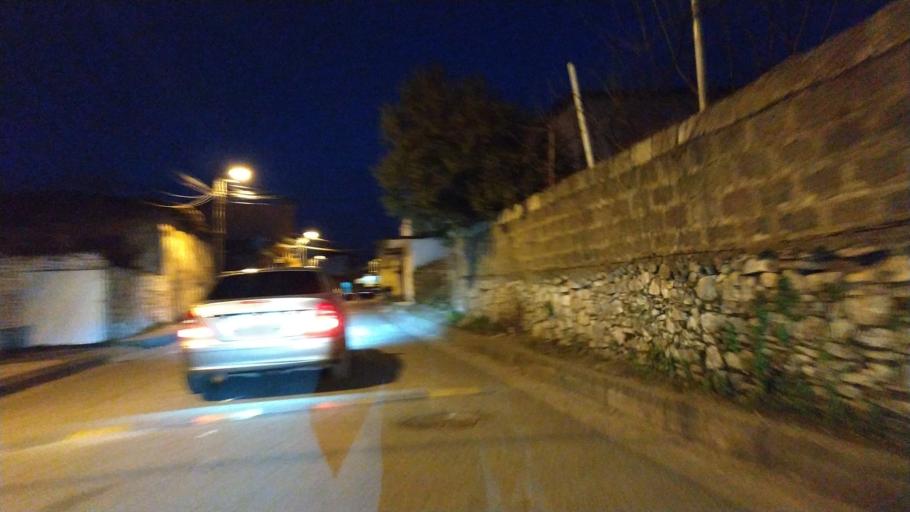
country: AL
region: Shkoder
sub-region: Rrethi i Shkodres
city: Shkoder
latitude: 42.0608
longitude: 19.5024
